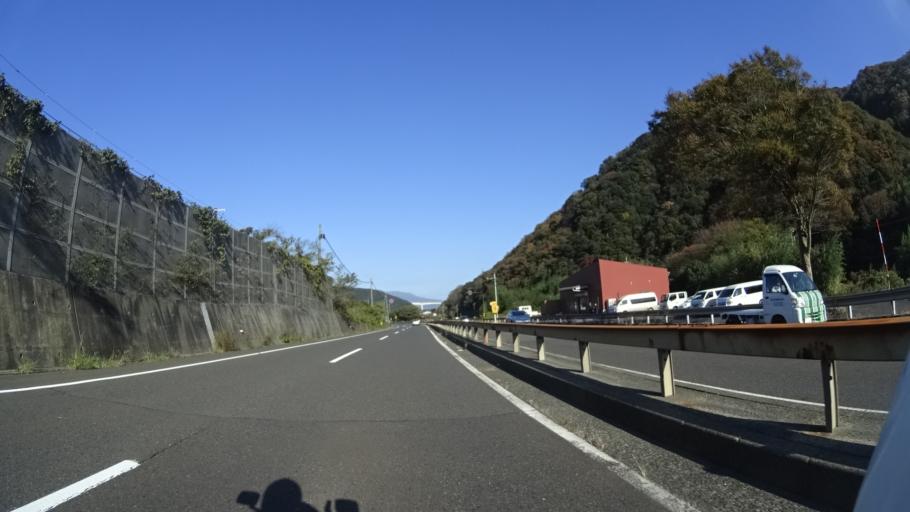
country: JP
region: Fukui
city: Tsuruga
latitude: 35.6072
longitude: 136.0882
